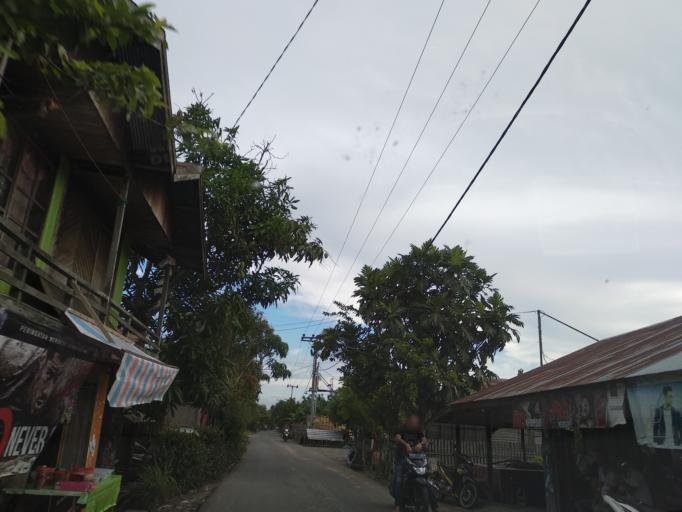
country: ID
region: South Kalimantan
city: Aluhaluh
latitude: -3.4352
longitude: 114.5934
